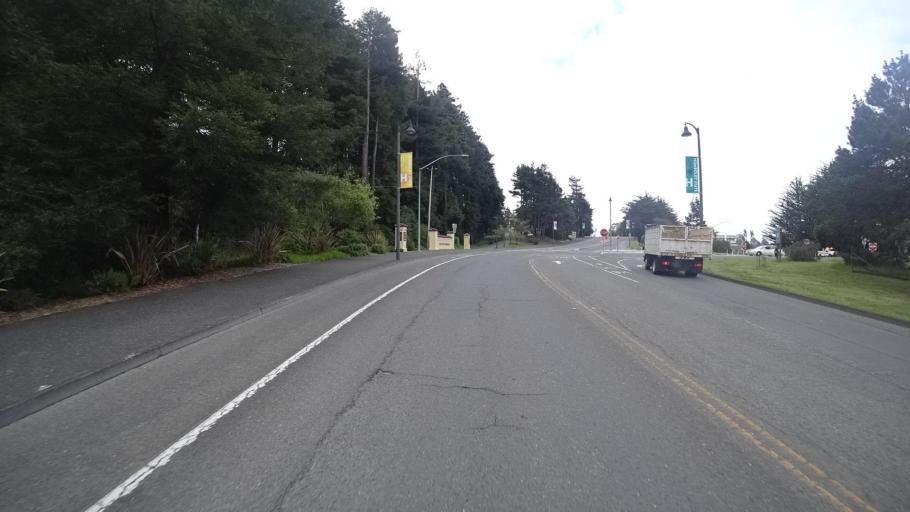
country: US
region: California
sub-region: Humboldt County
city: Arcata
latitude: 40.8791
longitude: -124.0809
